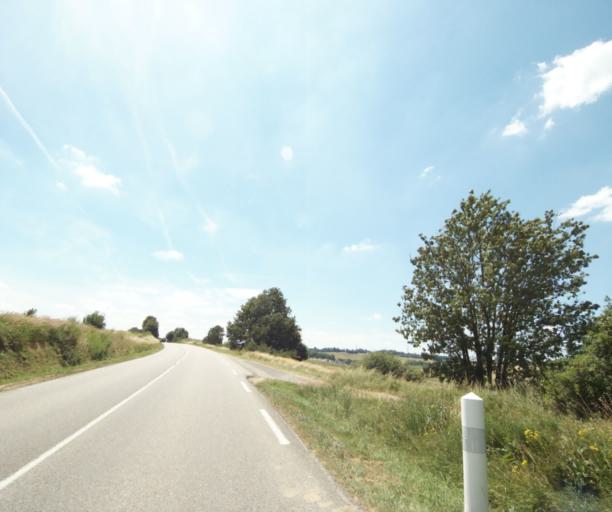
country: FR
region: Lorraine
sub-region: Departement de Meurthe-et-Moselle
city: Luneville
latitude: 48.6212
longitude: 6.4868
